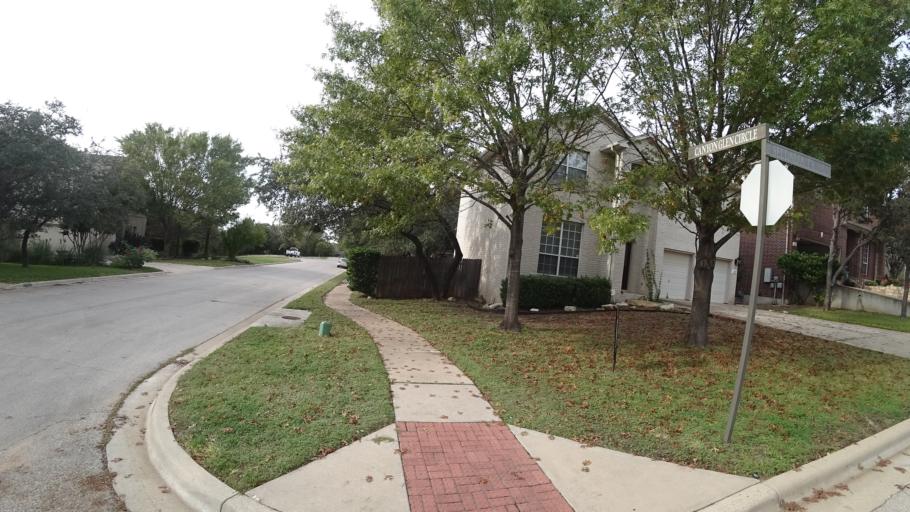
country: US
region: Texas
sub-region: Travis County
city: Hudson Bend
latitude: 30.3820
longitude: -97.8896
